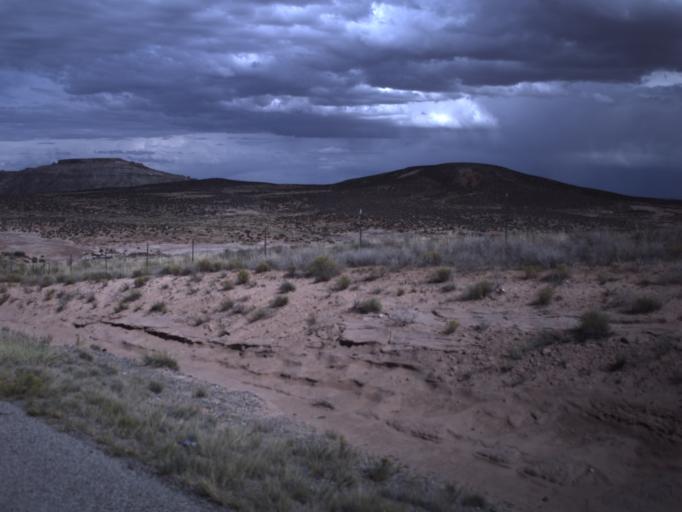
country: US
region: Utah
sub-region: San Juan County
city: Blanding
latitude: 37.2927
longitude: -109.4878
